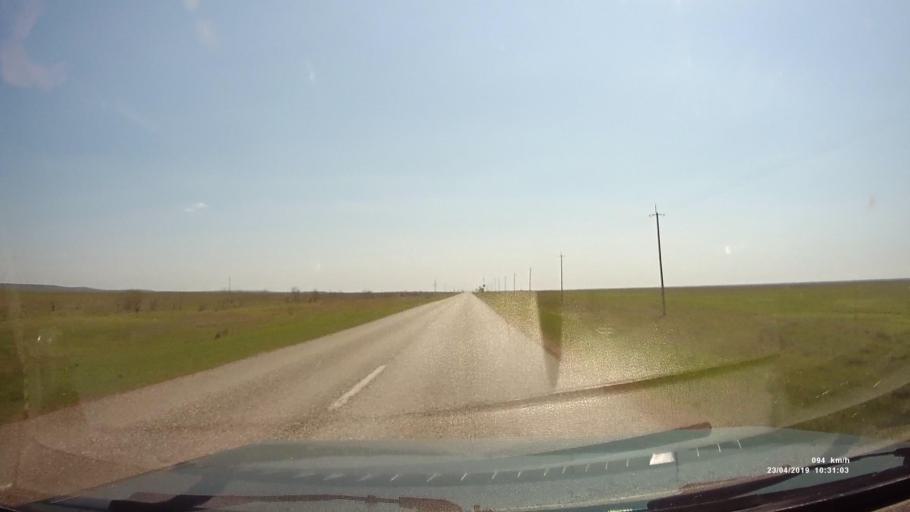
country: RU
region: Kalmykiya
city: Yashalta
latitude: 46.5881
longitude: 42.5557
